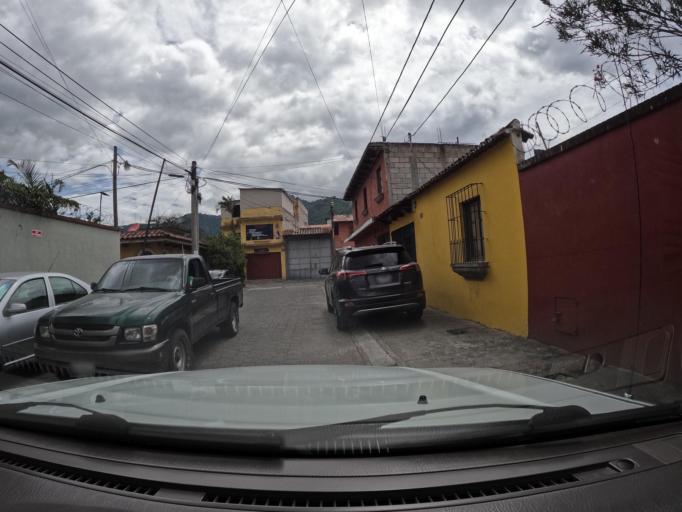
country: GT
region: Sacatepequez
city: Jocotenango
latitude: 14.5772
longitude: -90.7389
